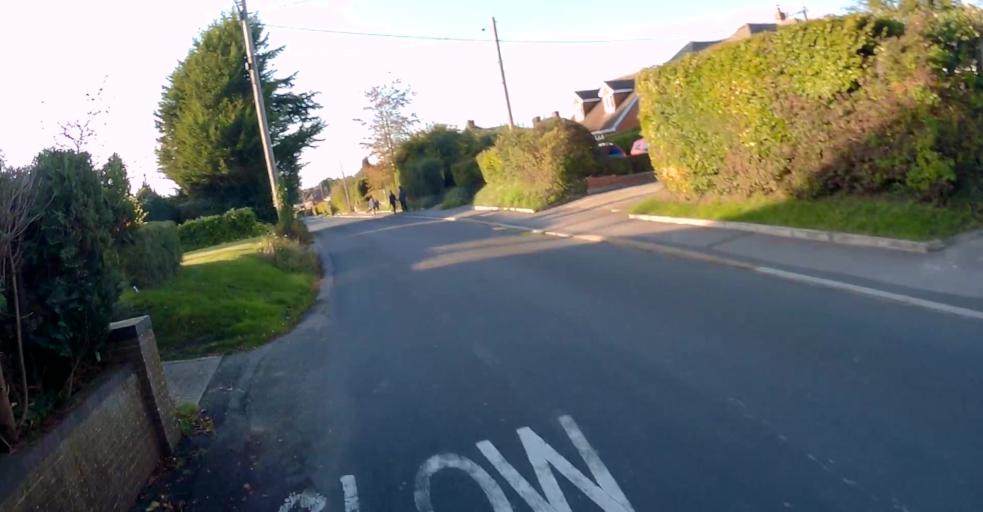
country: GB
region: England
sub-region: Hampshire
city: Old Basing
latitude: 51.2661
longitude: -1.0374
